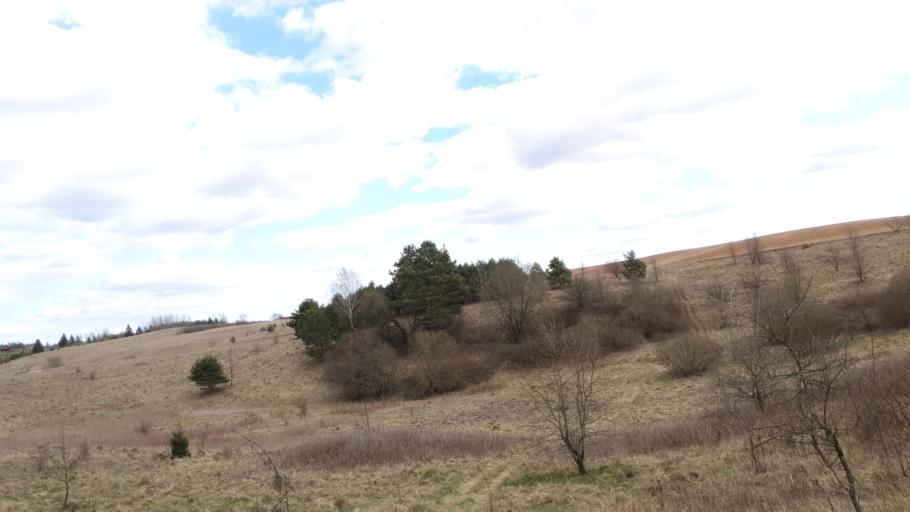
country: LT
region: Vilnius County
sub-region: Vilniaus Rajonas
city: Vievis
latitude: 54.6429
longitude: 24.7311
